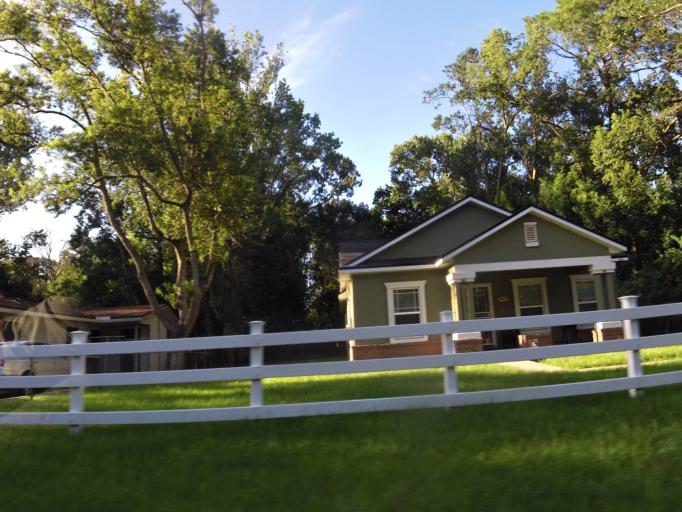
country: US
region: Florida
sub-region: Duval County
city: Jacksonville
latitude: 30.3435
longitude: -81.6945
